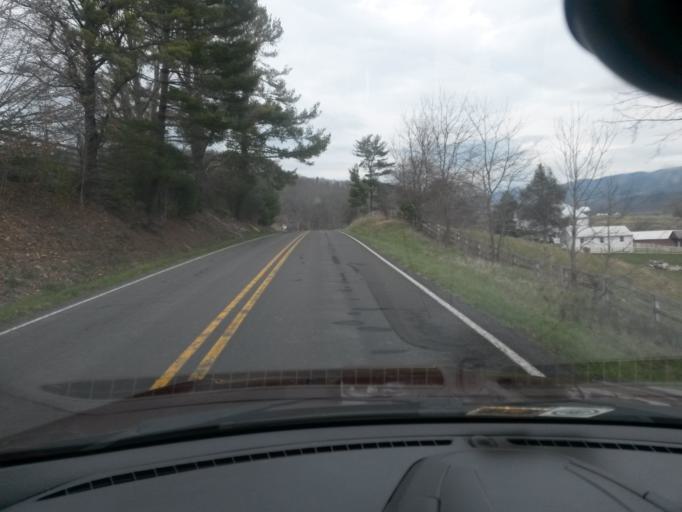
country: US
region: Virginia
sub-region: Bath County
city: Warm Springs
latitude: 38.2076
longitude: -79.7235
